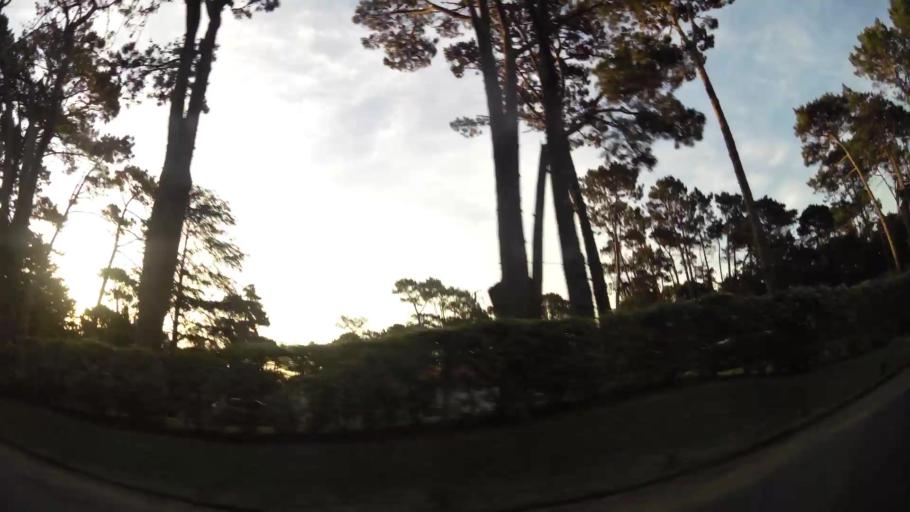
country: UY
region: Maldonado
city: Punta del Este
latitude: -34.9334
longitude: -54.9357
